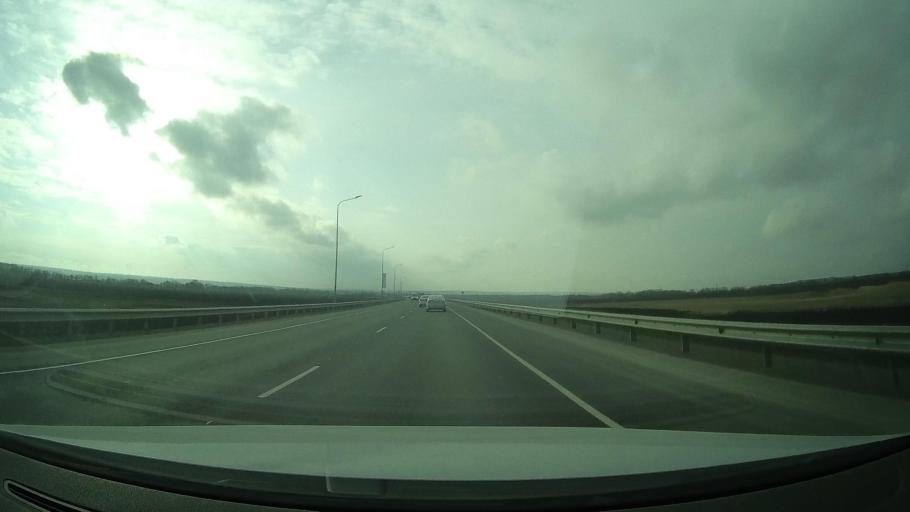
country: RU
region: Rostov
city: Grushevskaya
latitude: 47.4632
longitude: 39.8909
